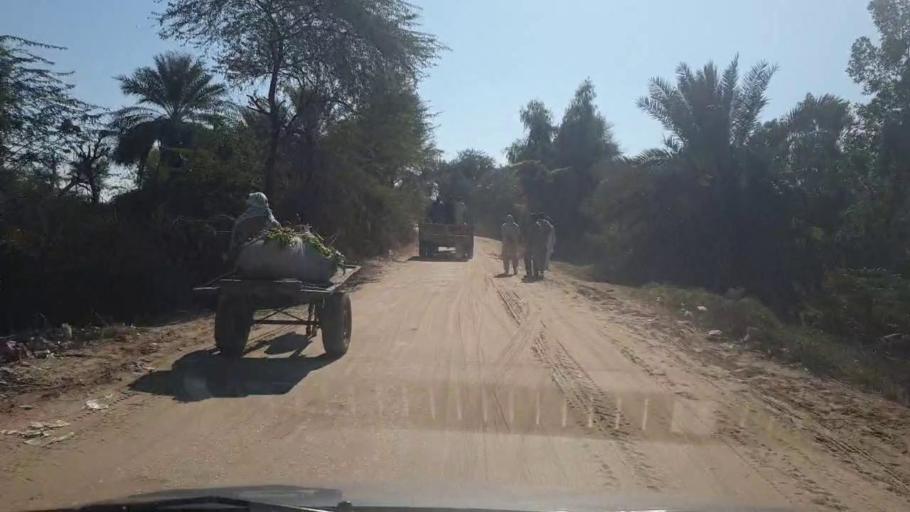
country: PK
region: Sindh
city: Bozdar
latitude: 27.0709
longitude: 68.6191
